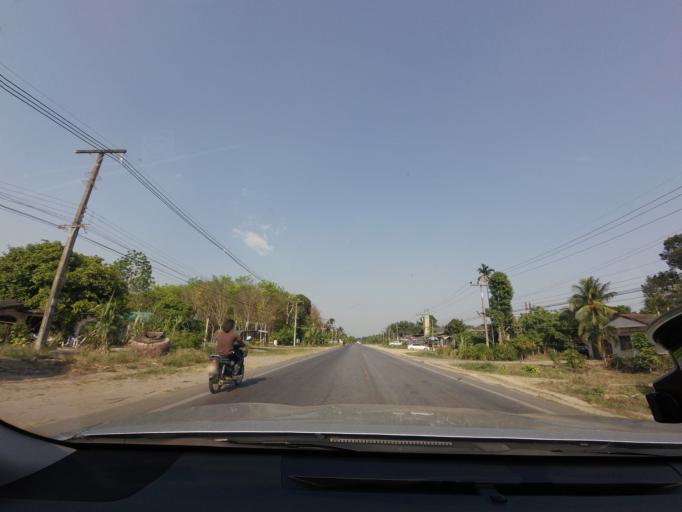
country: TH
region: Surat Thani
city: Phrasaeng
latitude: 8.5656
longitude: 99.1861
